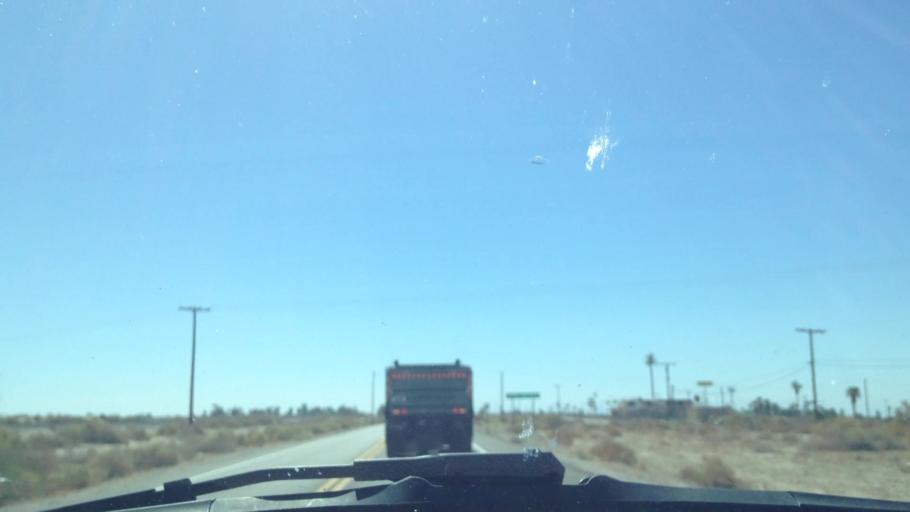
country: US
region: California
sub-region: Riverside County
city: Mecca
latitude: 33.5260
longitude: -115.9402
